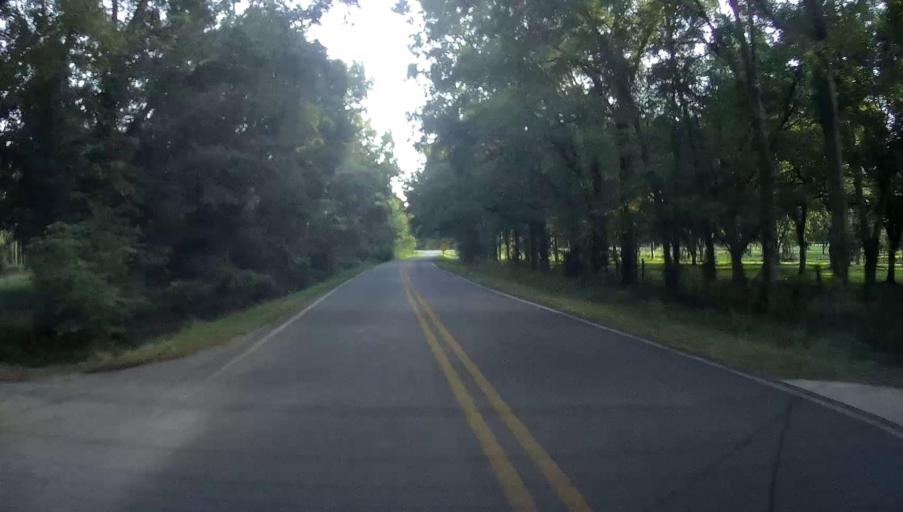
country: US
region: Georgia
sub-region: Pulaski County
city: Hawkinsville
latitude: 32.2703
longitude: -83.5382
